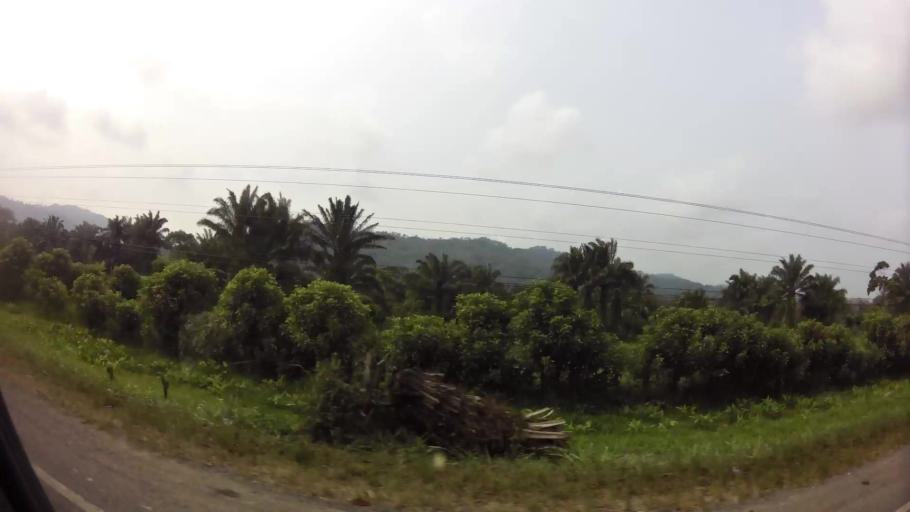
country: HN
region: Atlantida
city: Tela
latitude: 15.7668
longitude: -87.4638
